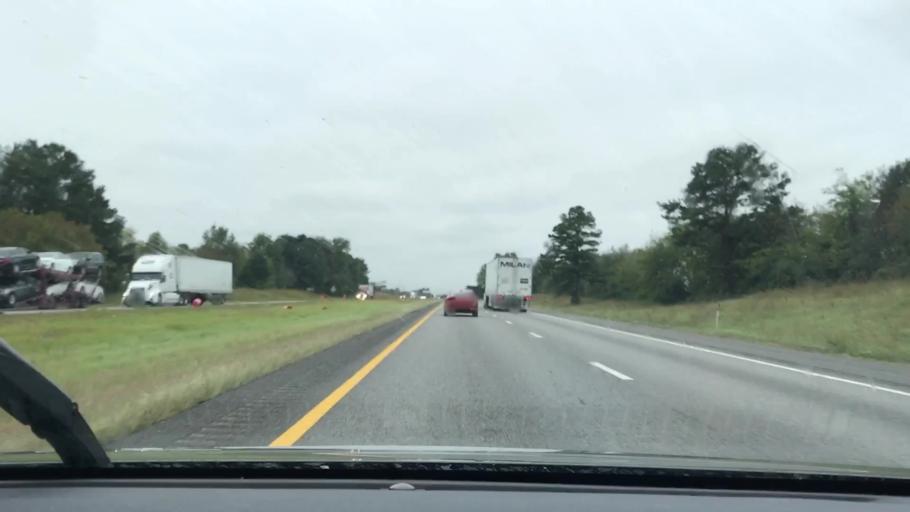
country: US
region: Tennessee
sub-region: Sumner County
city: Portland
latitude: 36.6182
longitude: -86.5779
